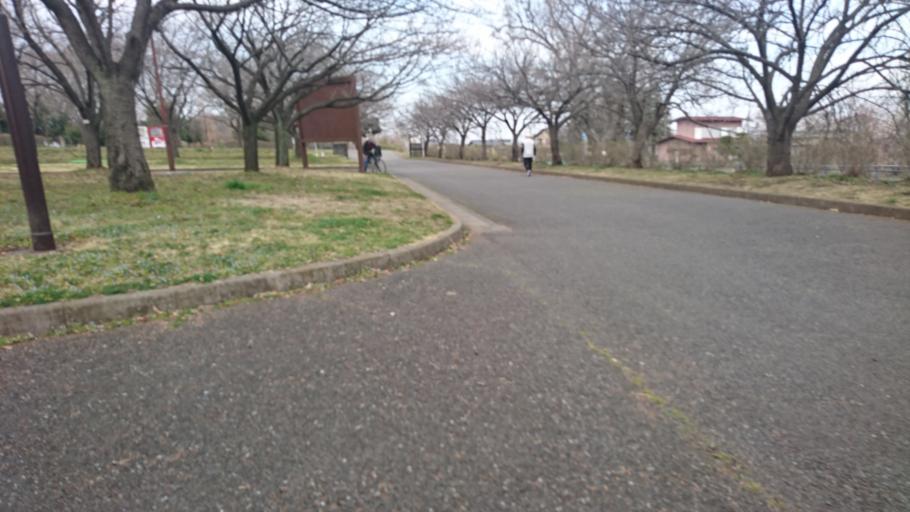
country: JP
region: Saitama
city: Kawagoe
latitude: 35.9150
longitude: 139.4529
